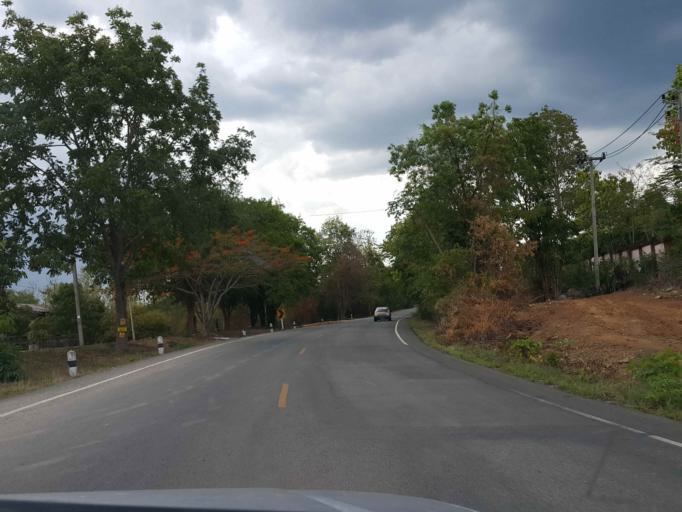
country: TH
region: Sukhothai
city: Thung Saliam
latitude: 17.3475
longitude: 99.4375
